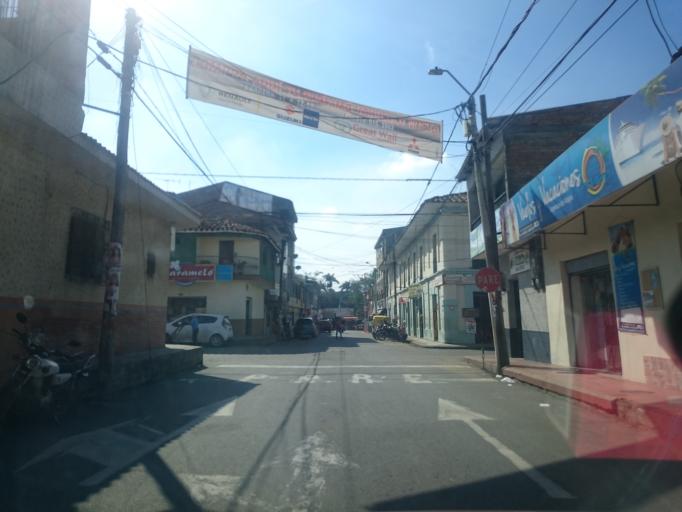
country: CO
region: Cauca
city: Santander de Quilichao
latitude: 3.0084
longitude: -76.4842
